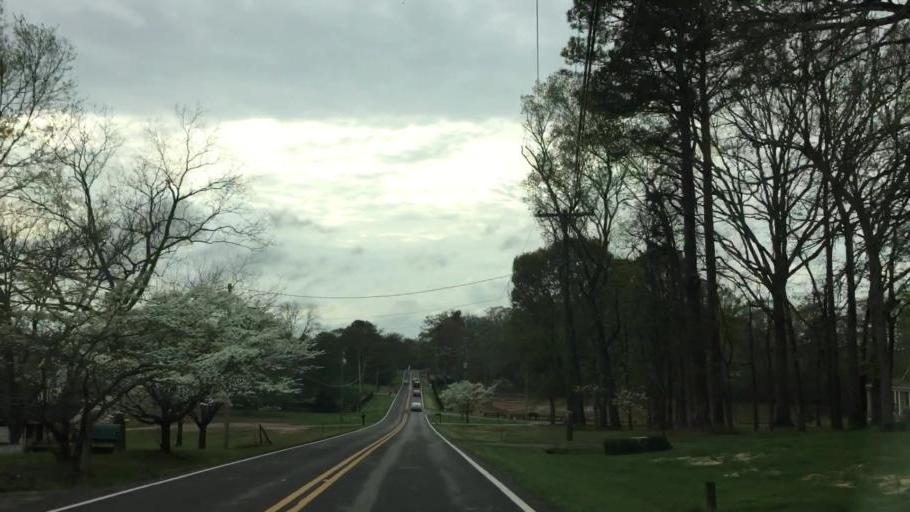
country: US
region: Georgia
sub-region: Fulton County
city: Milton
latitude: 34.1974
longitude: -84.3534
